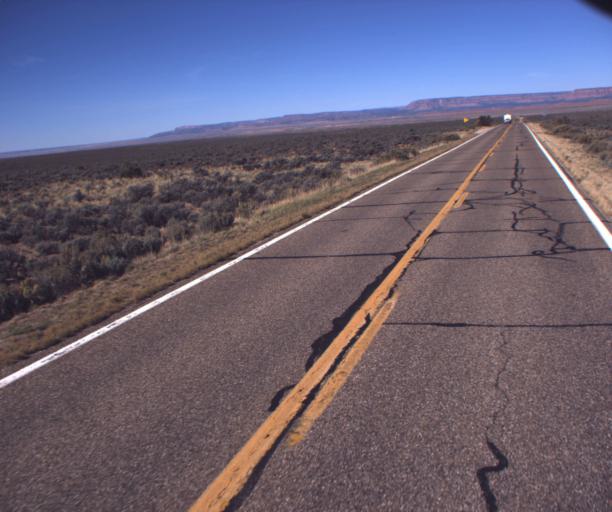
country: US
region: Arizona
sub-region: Coconino County
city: Fredonia
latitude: 36.8910
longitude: -112.3547
